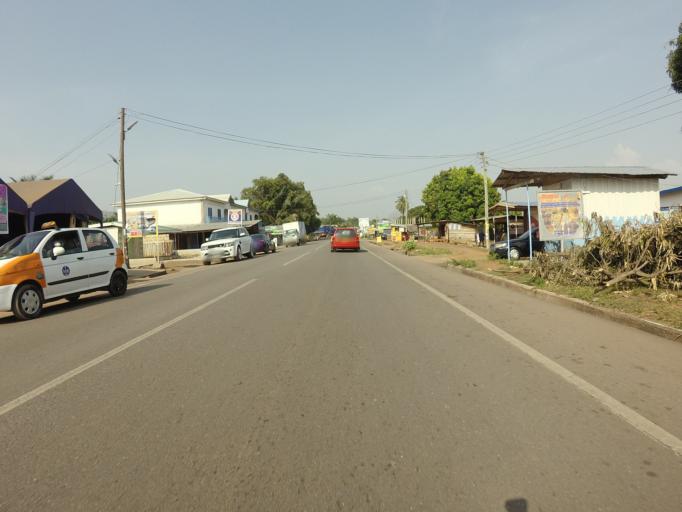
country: GH
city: Akropong
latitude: 6.1138
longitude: -0.0058
